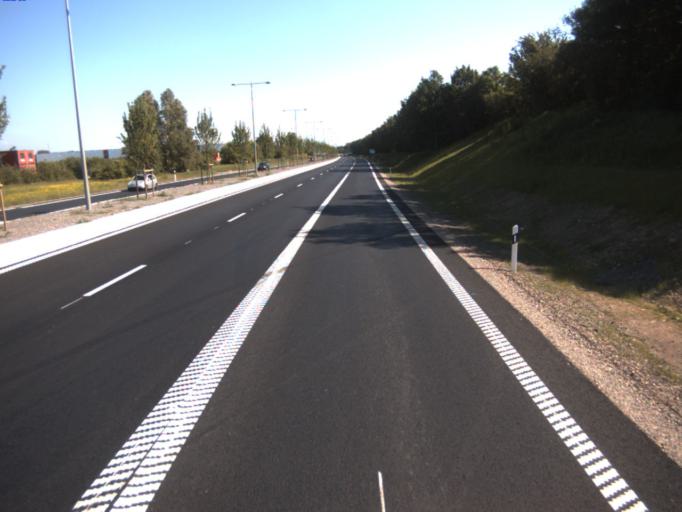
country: SE
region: Skane
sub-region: Helsingborg
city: Odakra
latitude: 56.0712
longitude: 12.7408
